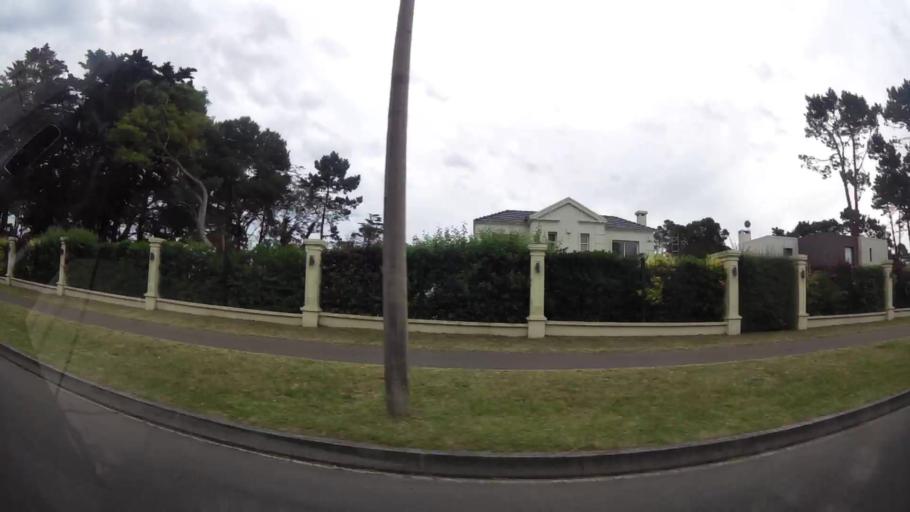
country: UY
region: Maldonado
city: Punta del Este
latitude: -34.9389
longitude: -54.9375
